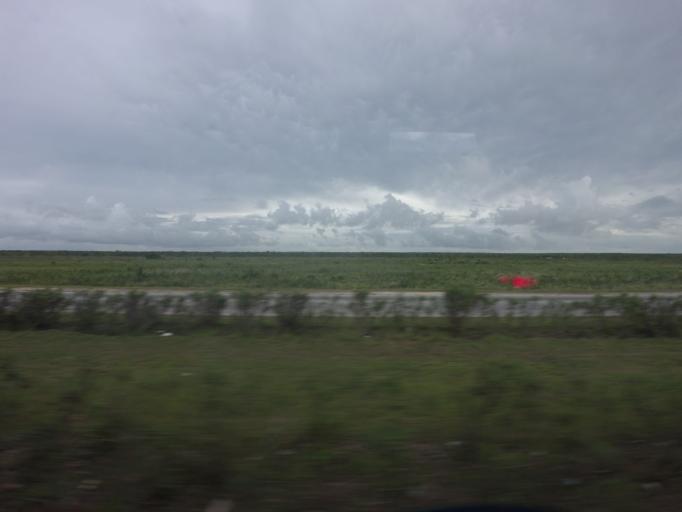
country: CU
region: Matanzas
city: Varadero
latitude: 23.1003
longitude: -81.4045
